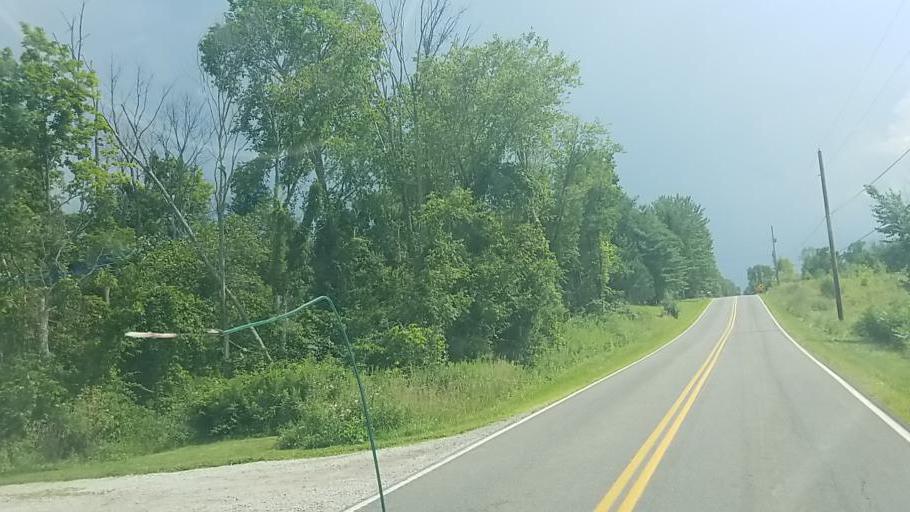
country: US
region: Ohio
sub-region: Medina County
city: Lodi
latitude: 41.0797
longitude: -82.0046
